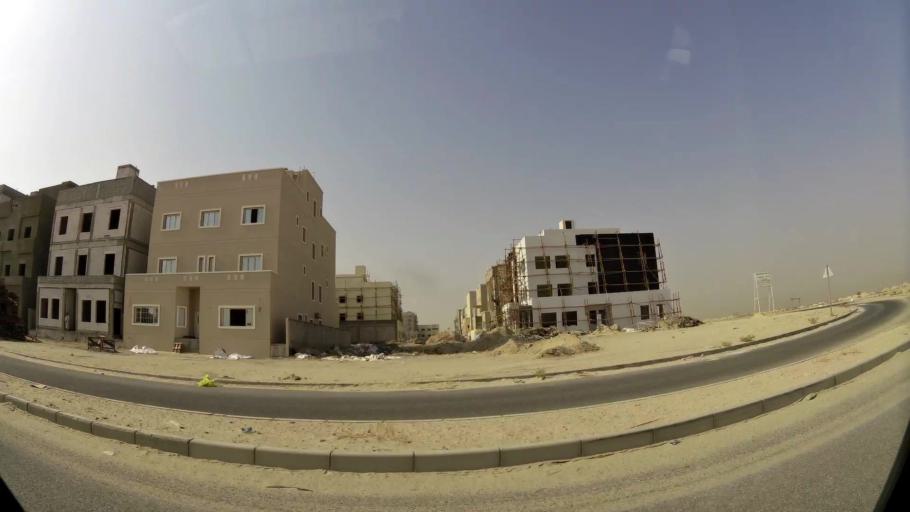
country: KW
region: Muhafazat al Jahra'
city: Al Jahra'
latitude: 29.3583
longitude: 47.7488
